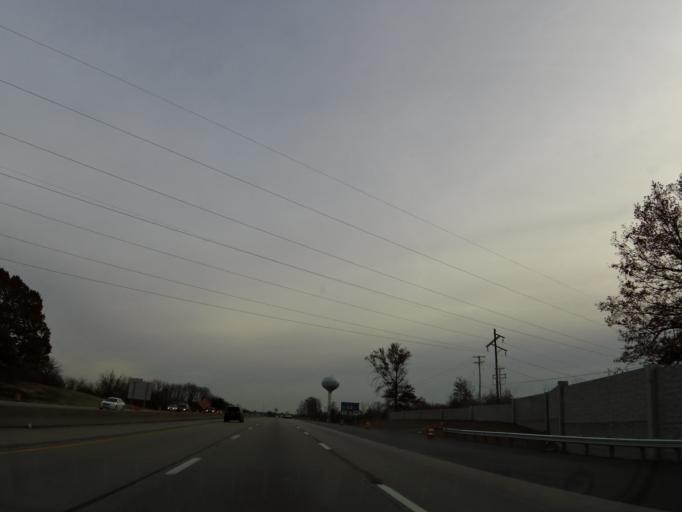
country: US
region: Kentucky
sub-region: Scott County
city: Georgetown
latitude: 38.2365
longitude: -84.5431
